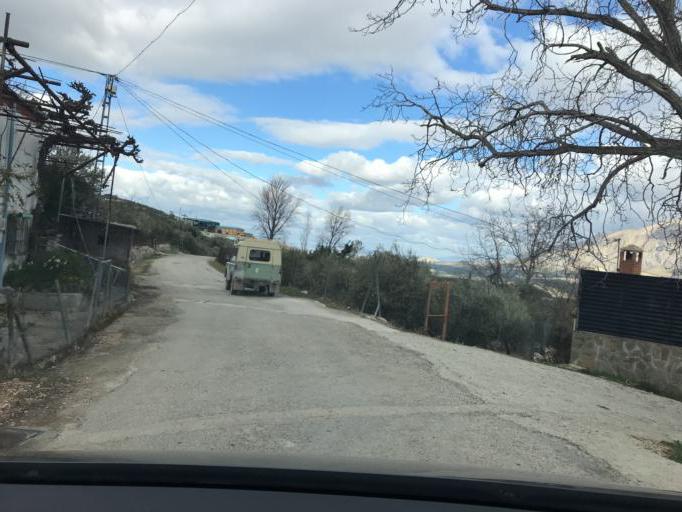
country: ES
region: Andalusia
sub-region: Provincia de Jaen
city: Jimena
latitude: 37.8012
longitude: -3.4614
